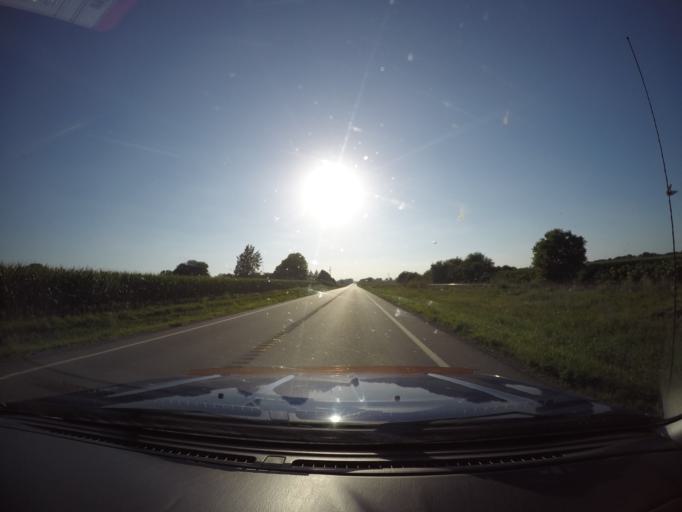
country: US
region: Kansas
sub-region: Shawnee County
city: Silver Lake
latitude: 39.1140
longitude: -95.8943
